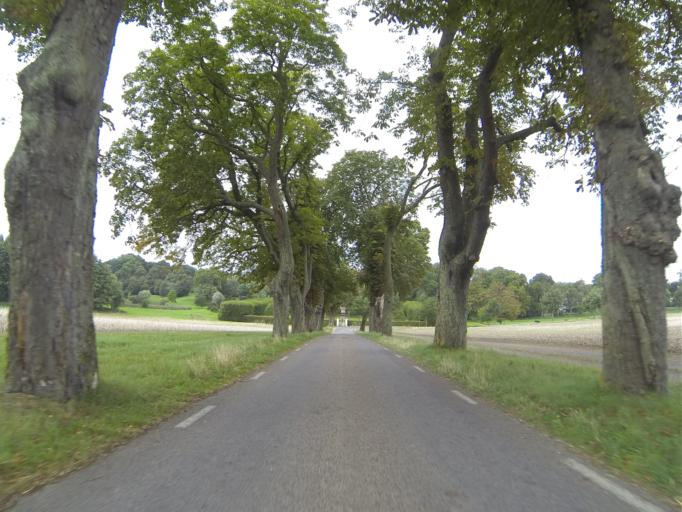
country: SE
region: Skane
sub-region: Eslovs Kommun
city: Eslov
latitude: 55.7650
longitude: 13.2597
